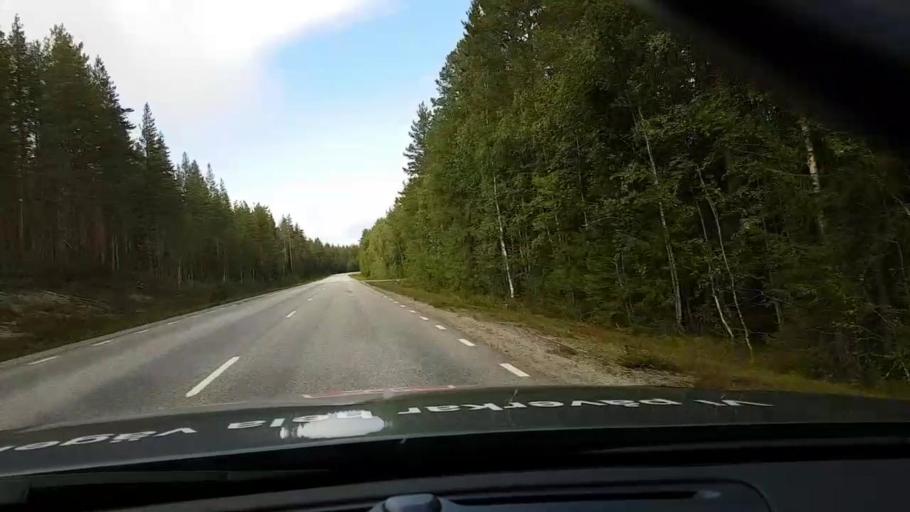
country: SE
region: Vaesternorrland
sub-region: OErnskoeldsviks Kommun
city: Bredbyn
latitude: 63.6019
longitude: 17.9069
